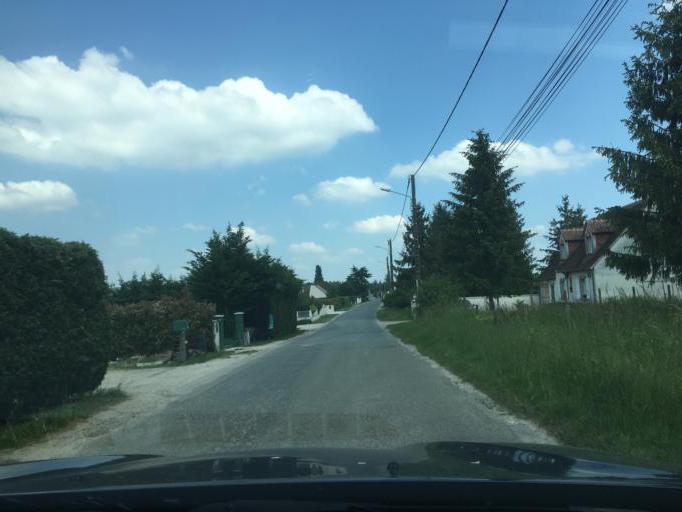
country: FR
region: Centre
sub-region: Departement du Loiret
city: Trainou
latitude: 47.9817
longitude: 2.1059
